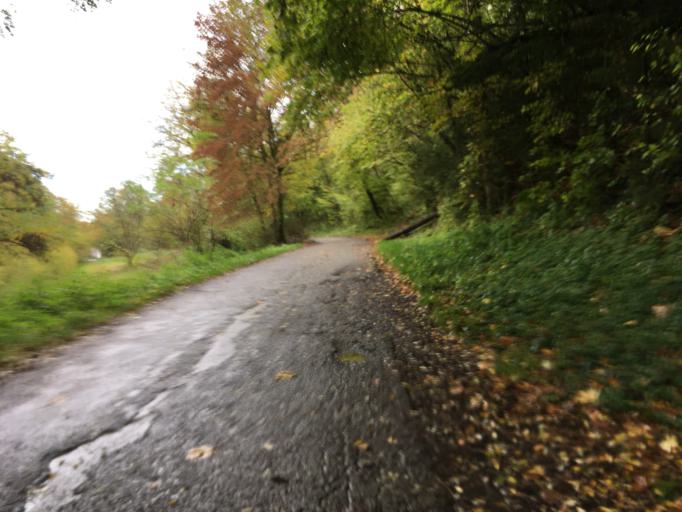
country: DE
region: Baden-Wuerttemberg
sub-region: Regierungsbezirk Stuttgart
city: Widdern
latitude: 49.3119
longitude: 9.4115
